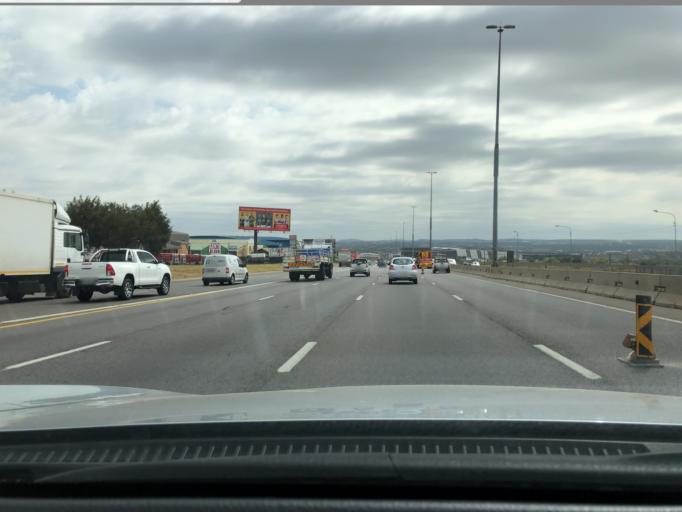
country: ZA
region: Gauteng
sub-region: City of Tshwane Metropolitan Municipality
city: Centurion
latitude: -25.9029
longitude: 28.1611
